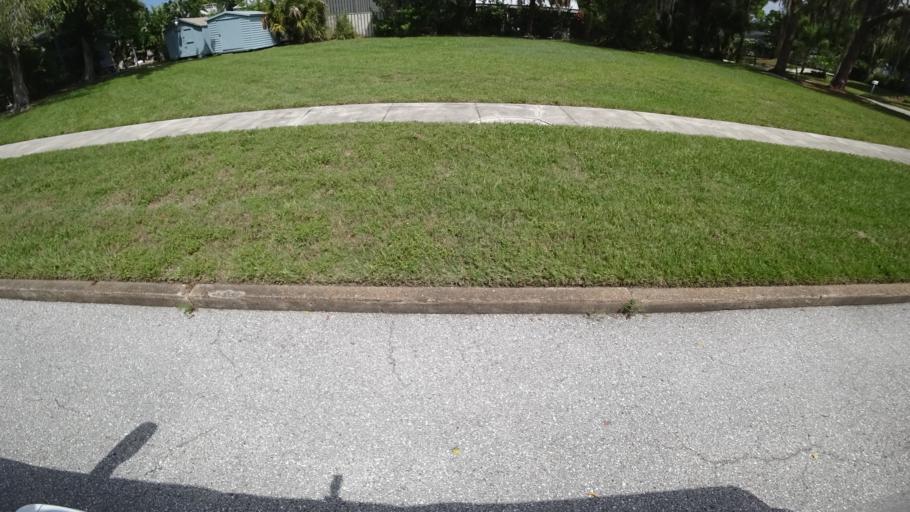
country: US
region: Florida
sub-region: Manatee County
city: Whitfield
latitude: 27.4089
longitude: -82.5760
